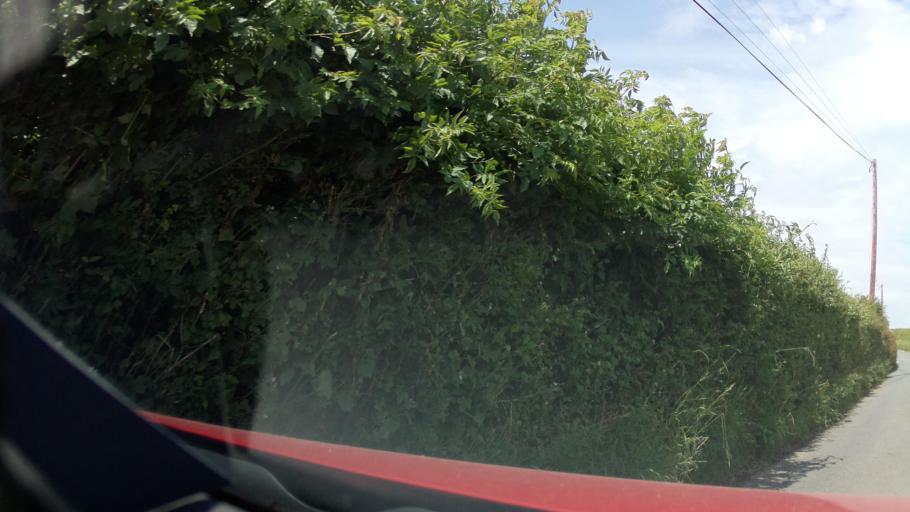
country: GB
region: Wales
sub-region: Vale of Glamorgan
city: Wick
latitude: 51.4167
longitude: -3.5483
